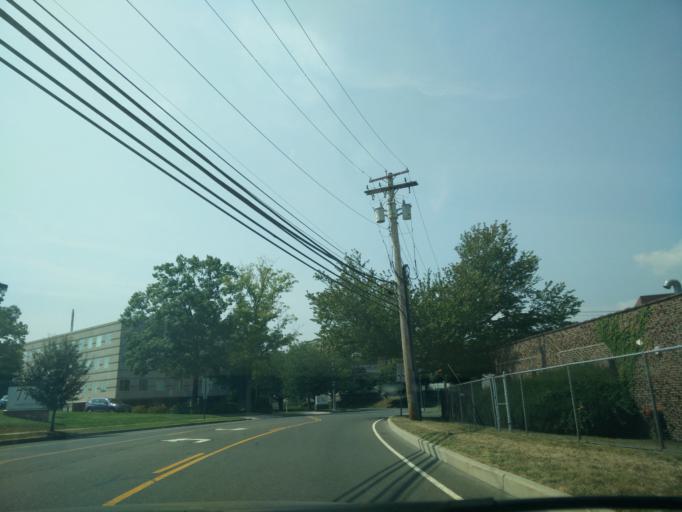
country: US
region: Connecticut
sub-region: Fairfield County
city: Bridgeport
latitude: 41.1627
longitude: -73.2347
